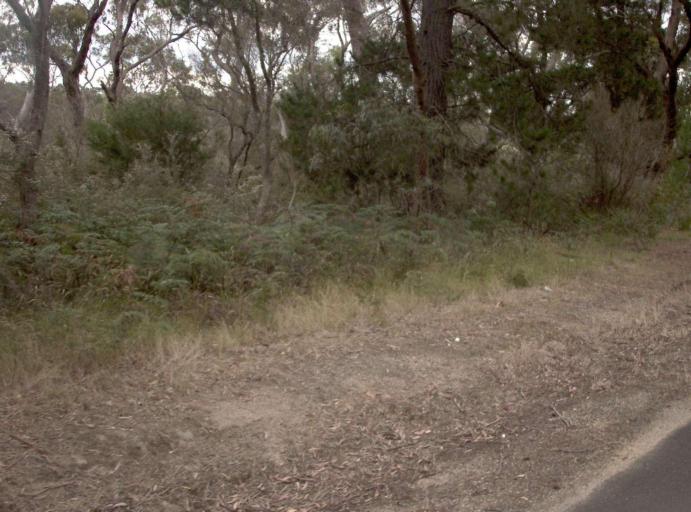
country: AU
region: Victoria
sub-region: Wellington
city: Sale
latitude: -38.2130
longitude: 147.0637
